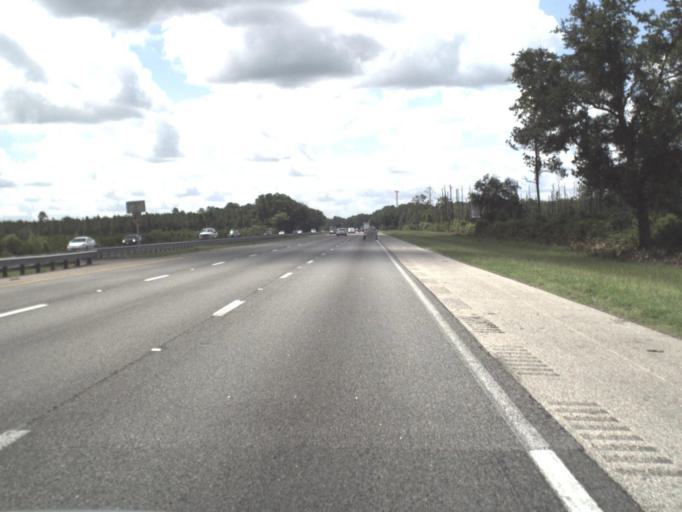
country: US
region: Florida
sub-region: Saint Johns County
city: Saint Augustine Shores
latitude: 29.6950
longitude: -81.3255
